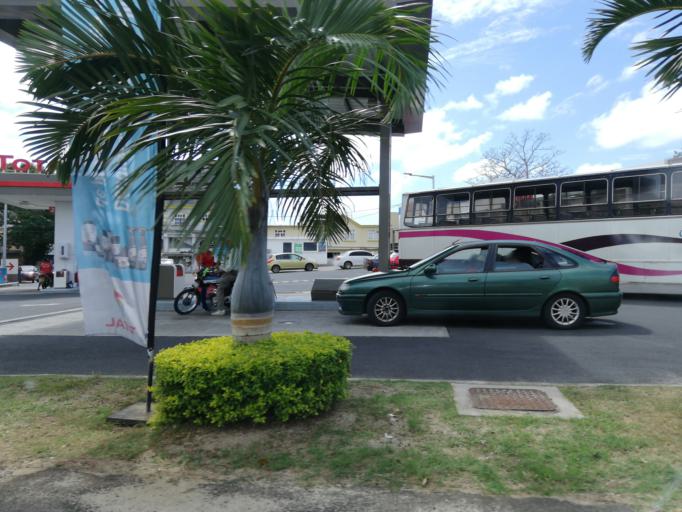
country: MU
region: Flacq
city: Centre de Flacq
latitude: -20.1989
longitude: 57.7214
